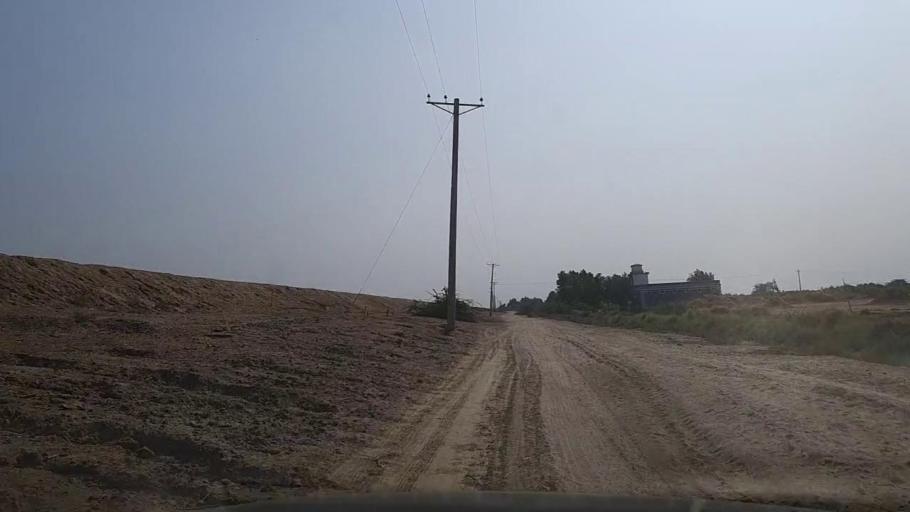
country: PK
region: Sindh
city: Chuhar Jamali
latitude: 24.5585
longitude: 67.9151
